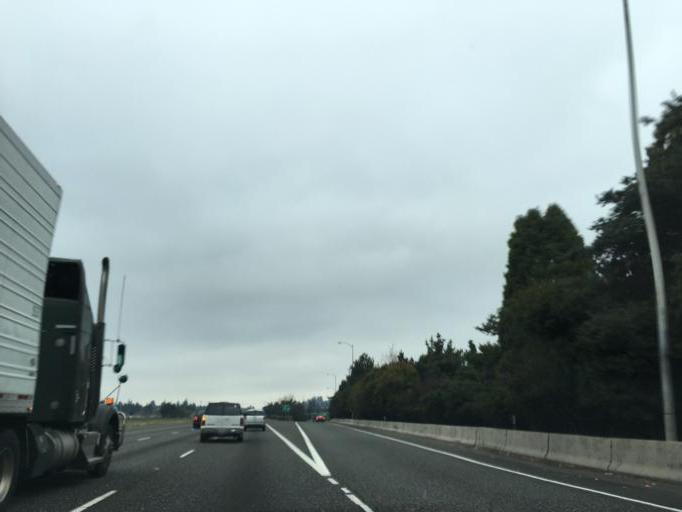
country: US
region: Oregon
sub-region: Multnomah County
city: Lents
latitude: 45.4737
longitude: -122.5653
